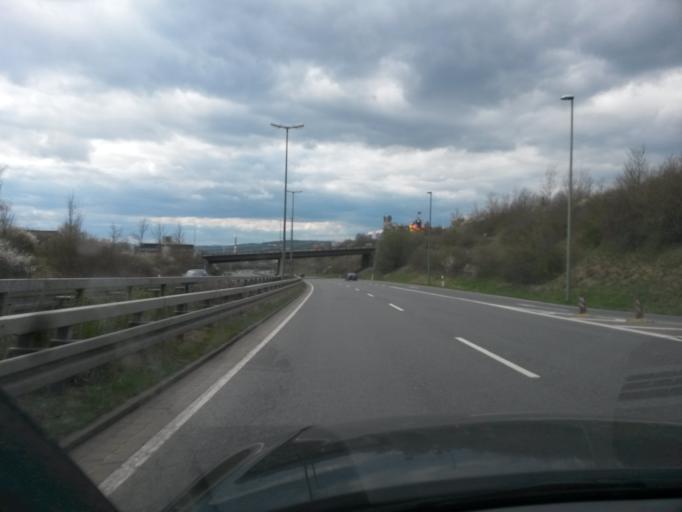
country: DE
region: Bavaria
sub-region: Regierungsbezirk Unterfranken
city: Gerbrunn
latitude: 49.7965
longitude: 9.9891
